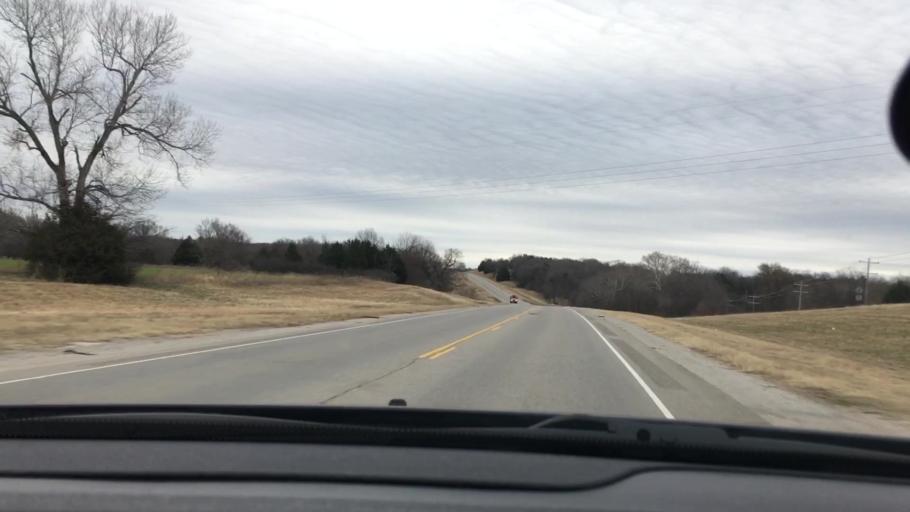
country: US
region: Oklahoma
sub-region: Johnston County
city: Tishomingo
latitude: 34.2341
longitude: -96.7849
